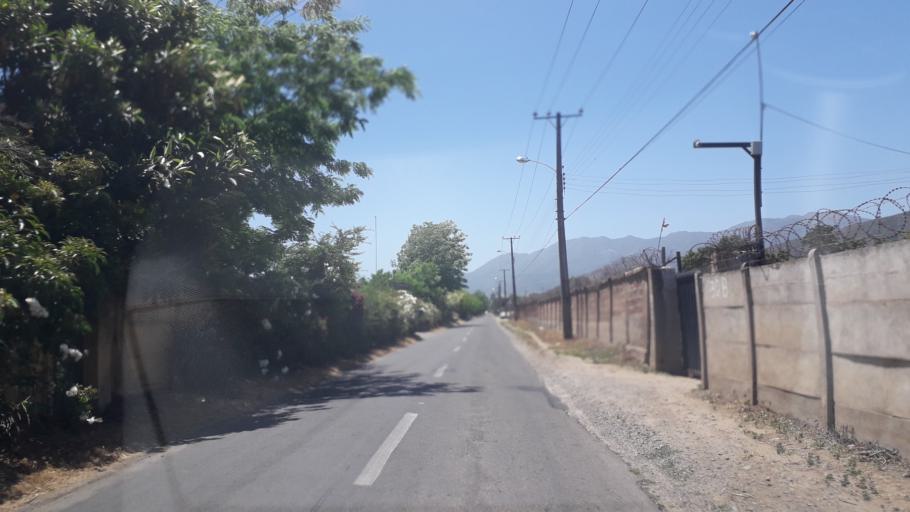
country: CL
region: Valparaiso
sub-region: Provincia de Quillota
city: Quillota
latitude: -32.9227
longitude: -71.2438
